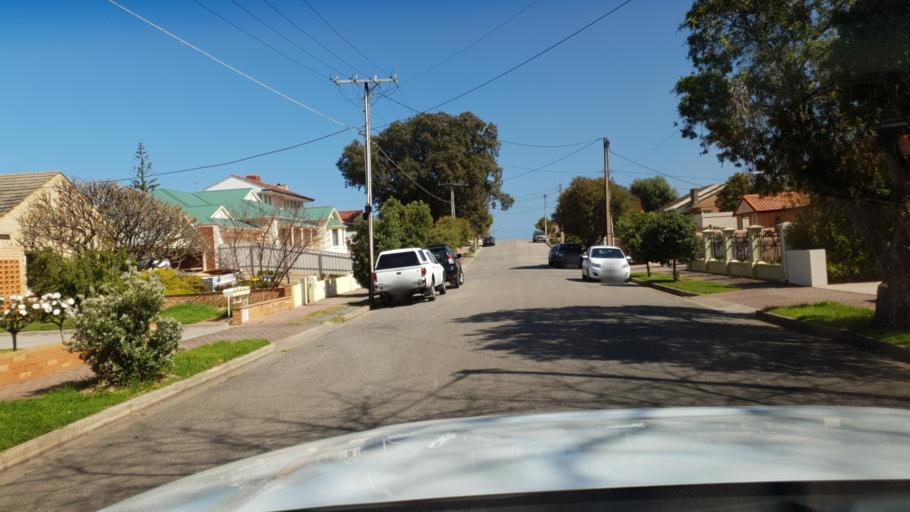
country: AU
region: South Australia
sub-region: Adelaide
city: Brighton
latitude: -35.0241
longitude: 138.5197
